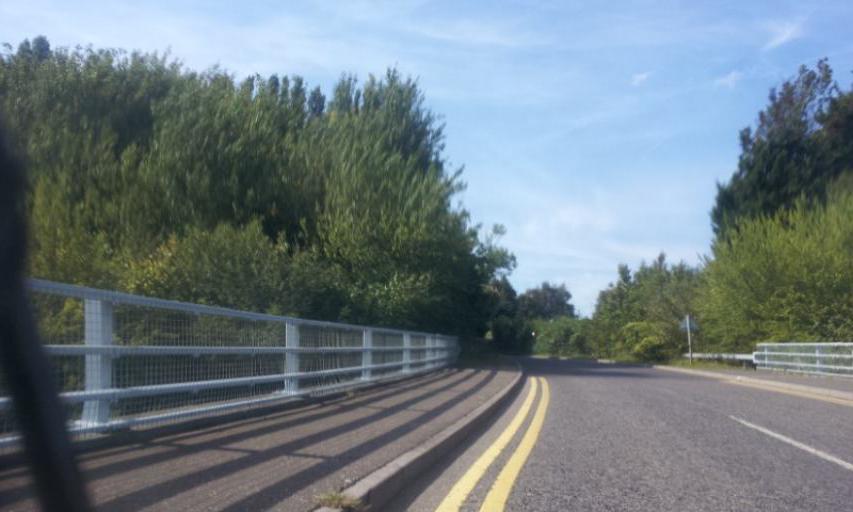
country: GB
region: England
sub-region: Kent
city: Newington
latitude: 51.3364
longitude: 0.6705
